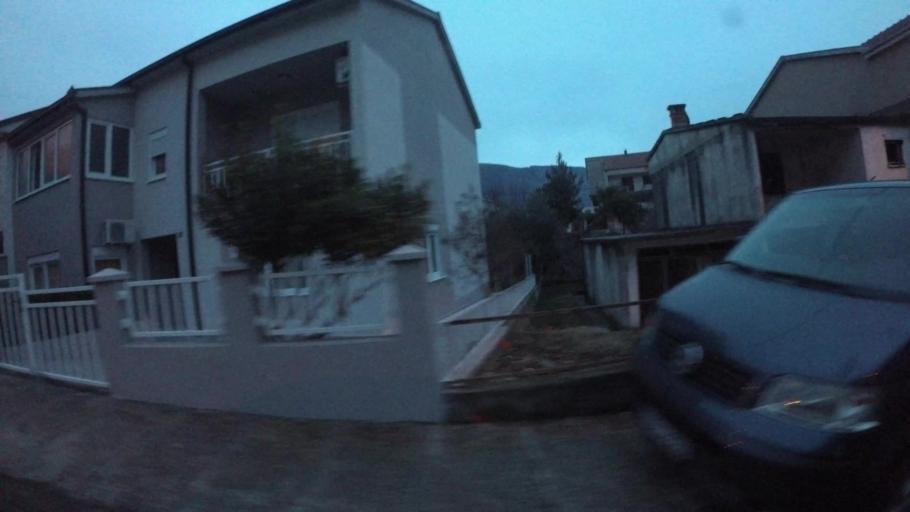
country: BA
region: Federation of Bosnia and Herzegovina
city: Rodoc
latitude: 43.3241
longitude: 17.8182
